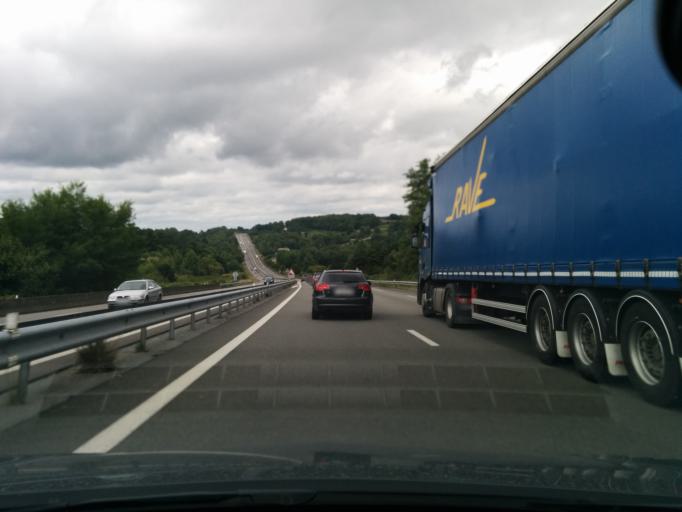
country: FR
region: Limousin
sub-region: Departement de la Haute-Vienne
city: Bessines-sur-Gartempe
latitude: 46.0676
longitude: 1.3609
